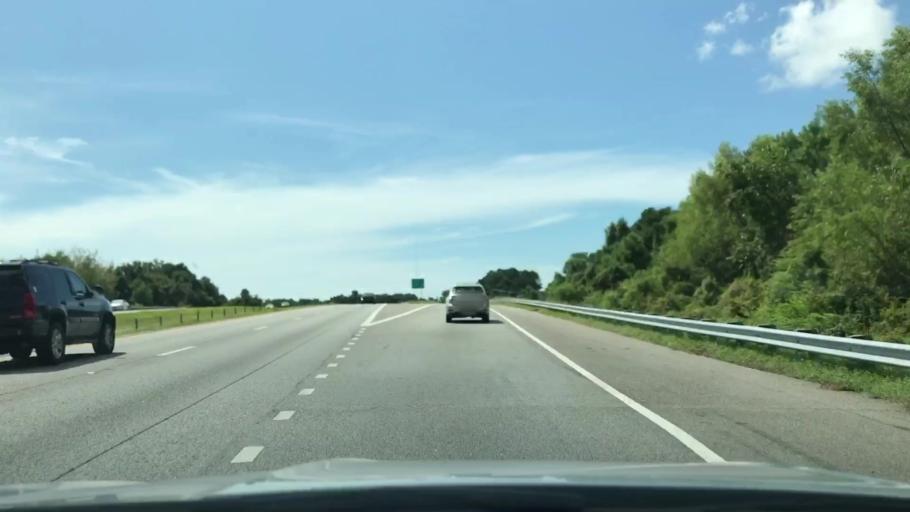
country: US
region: South Carolina
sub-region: Charleston County
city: Mount Pleasant
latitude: 32.8256
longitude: -79.8506
